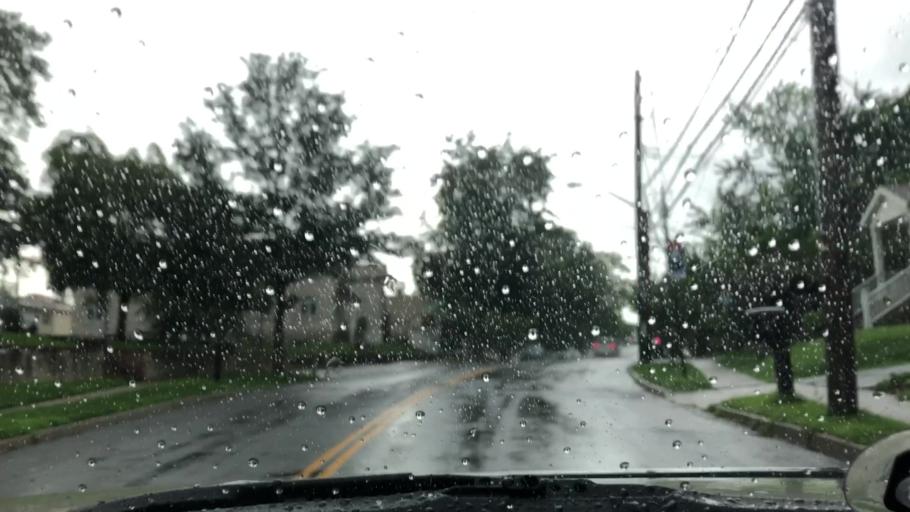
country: US
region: New Jersey
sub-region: Middlesex County
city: Carteret
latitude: 40.5293
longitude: -74.2025
